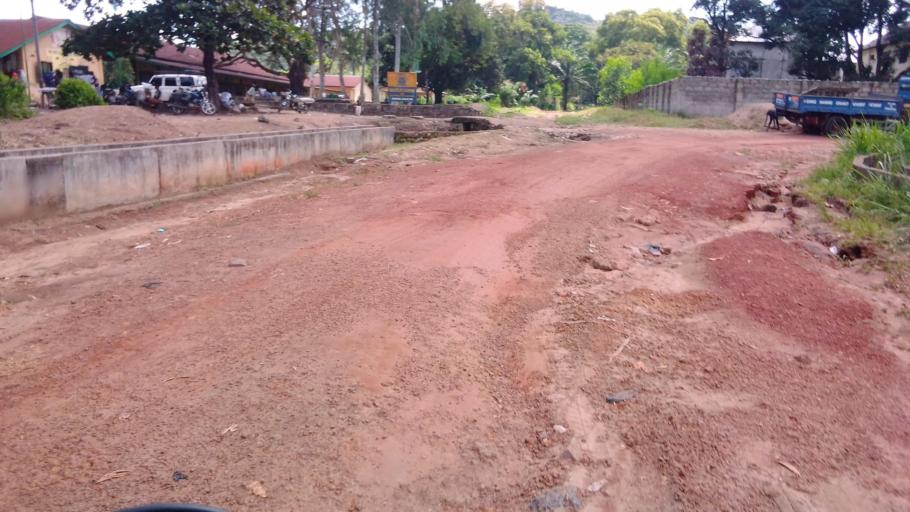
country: SL
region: Northern Province
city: Makeni
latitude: 8.8876
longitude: -12.0555
